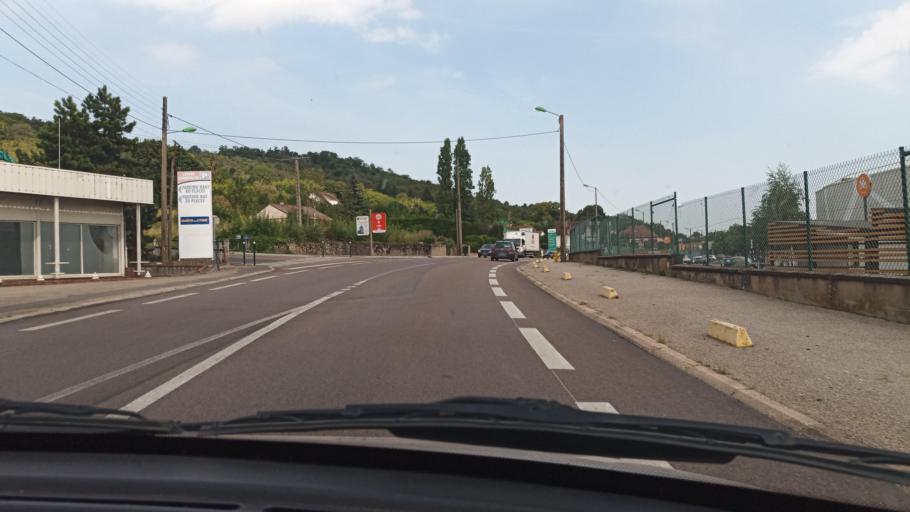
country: FR
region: Bourgogne
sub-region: Departement de l'Yonne
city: Saint-Martin-du-Tertre
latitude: 48.1992
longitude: 3.2644
